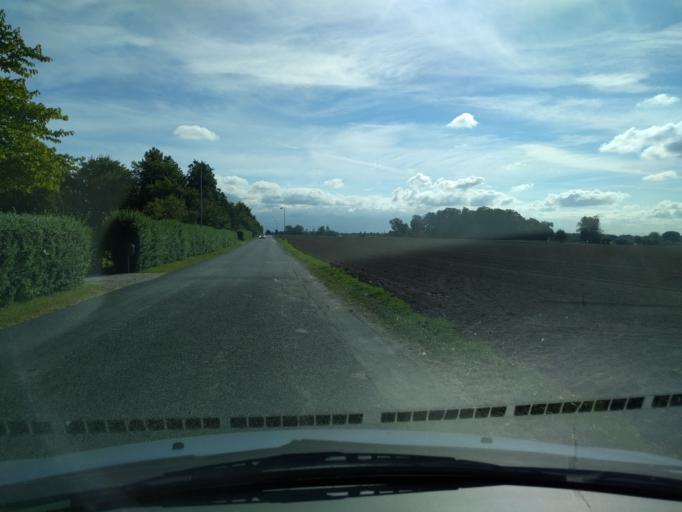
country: DK
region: South Denmark
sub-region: Kerteminde Kommune
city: Munkebo
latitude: 55.4166
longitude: 10.5746
